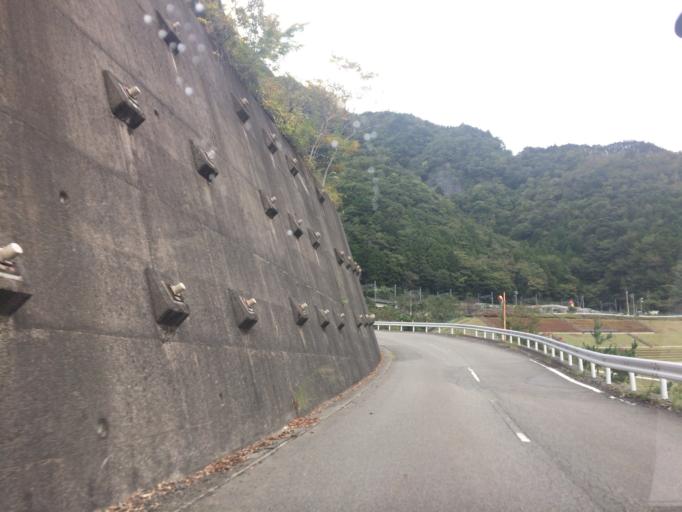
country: JP
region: Shizuoka
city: Shizuoka-shi
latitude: 35.1690
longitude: 138.1533
